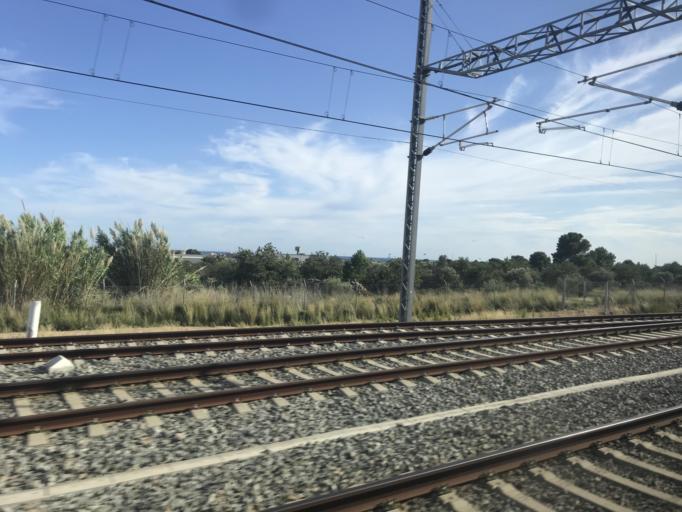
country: ES
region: Catalonia
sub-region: Provincia de Tarragona
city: Colldejou
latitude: 41.0023
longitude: 0.9148
